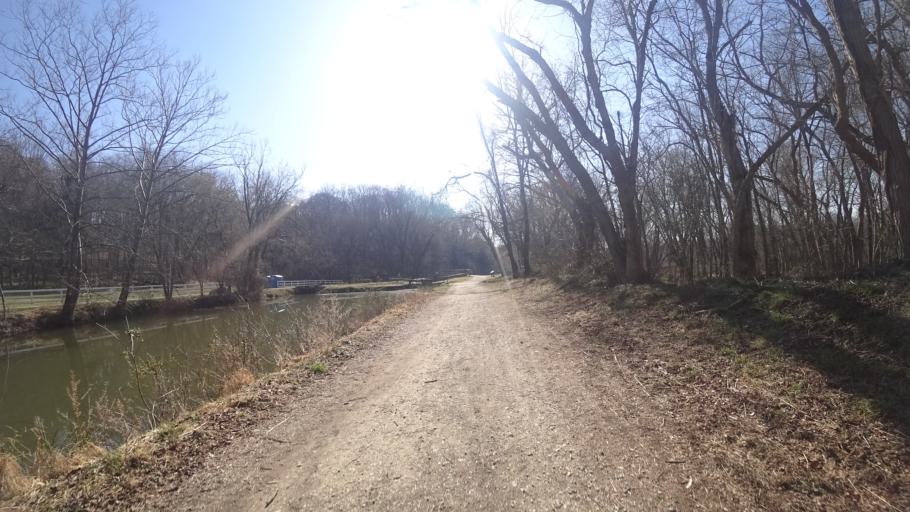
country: US
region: Maryland
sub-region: Montgomery County
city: Travilah
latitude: 39.0541
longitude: -77.2896
